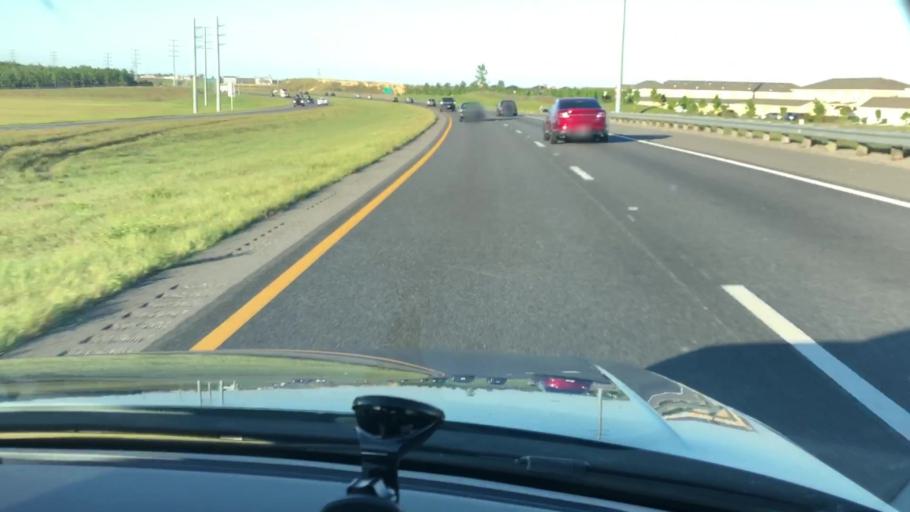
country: US
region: Florida
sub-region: Orange County
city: Oakland
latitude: 28.4622
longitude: -81.6330
